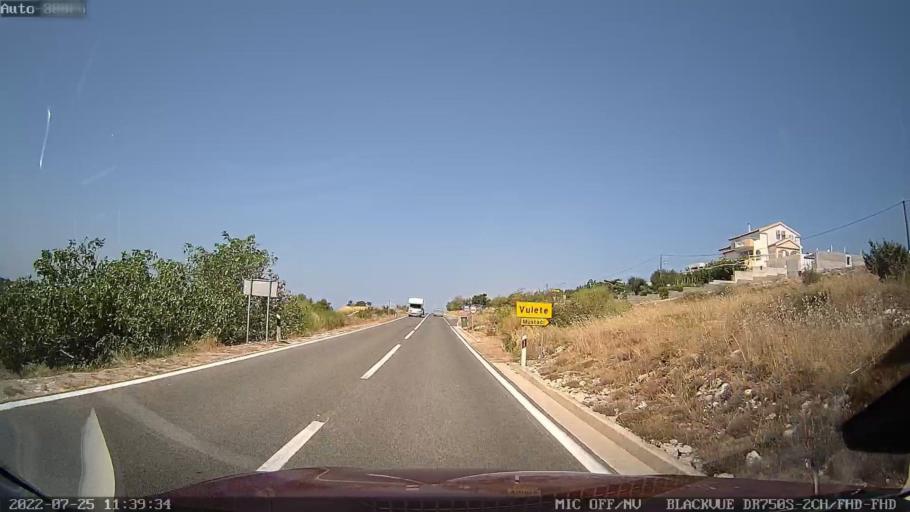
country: HR
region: Zadarska
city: Razanac
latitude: 44.2578
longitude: 15.3701
